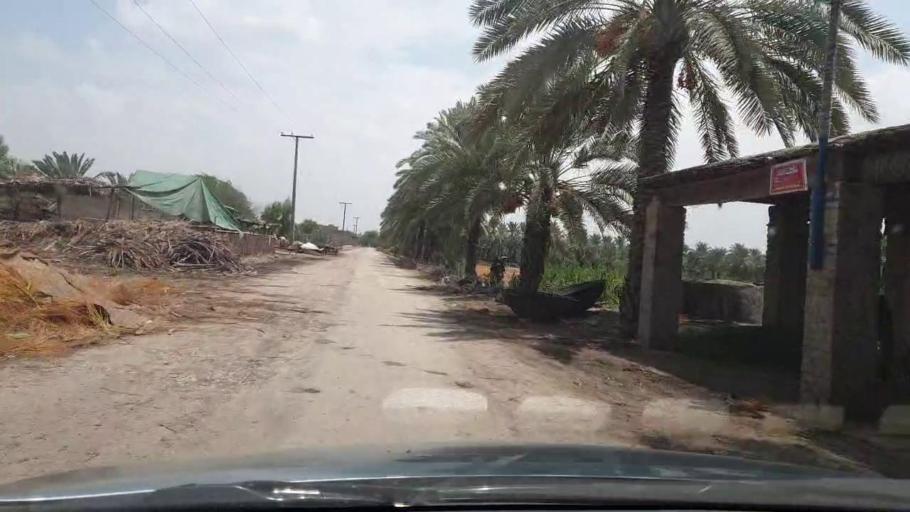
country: PK
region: Sindh
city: Khairpur
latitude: 27.4367
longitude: 68.7577
